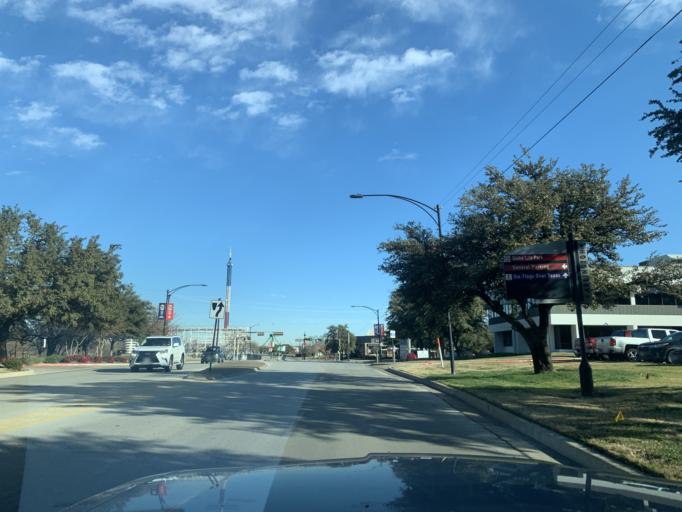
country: US
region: Texas
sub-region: Tarrant County
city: Arlington
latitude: 32.7514
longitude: -97.0685
